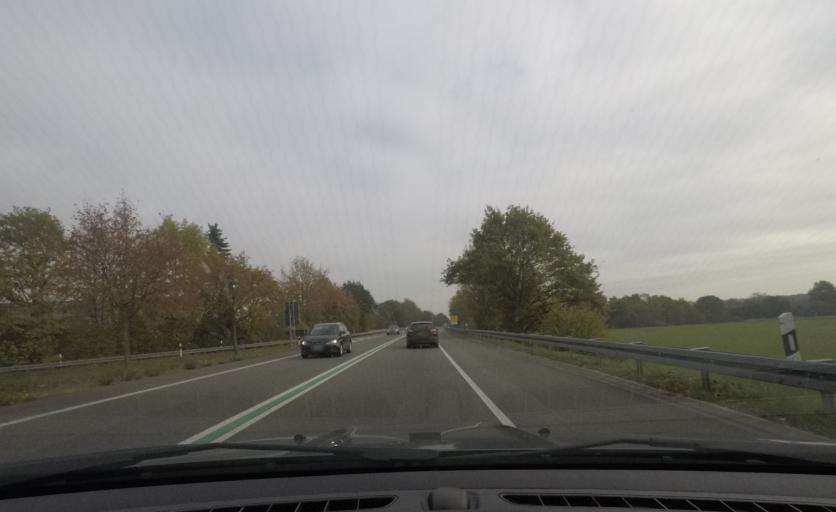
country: DE
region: North Rhine-Westphalia
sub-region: Regierungsbezirk Munster
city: Borken
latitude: 51.8377
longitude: 6.8781
